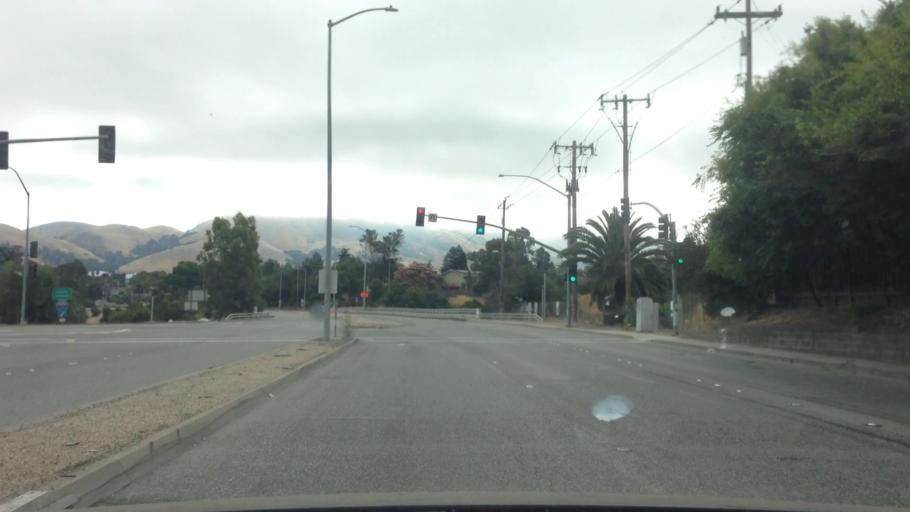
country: US
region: California
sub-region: Alameda County
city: Fremont
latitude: 37.5315
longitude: -121.9436
